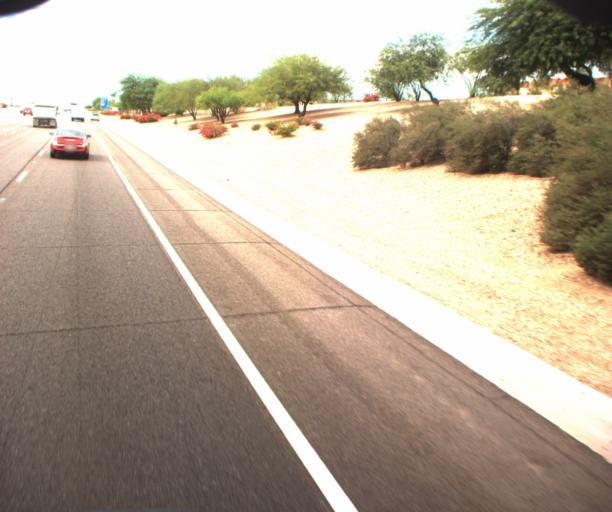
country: US
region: Arizona
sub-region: Maricopa County
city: Chandler
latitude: 33.2919
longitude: -111.9113
